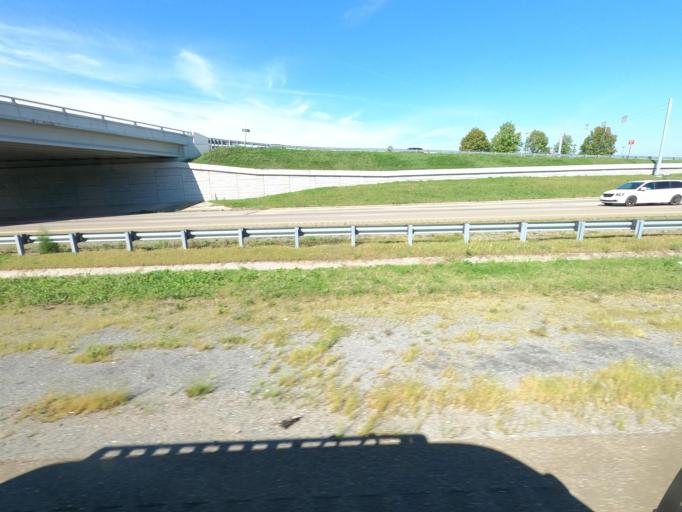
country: US
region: Tennessee
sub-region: Hamblen County
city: Morristown
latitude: 36.2143
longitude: -83.2607
